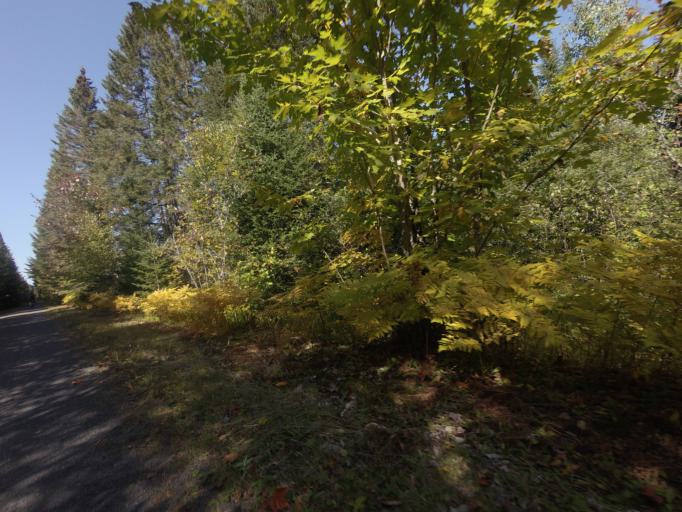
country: CA
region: Quebec
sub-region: Laurentides
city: Sainte-Agathe-des-Monts
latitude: 46.0942
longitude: -74.3493
